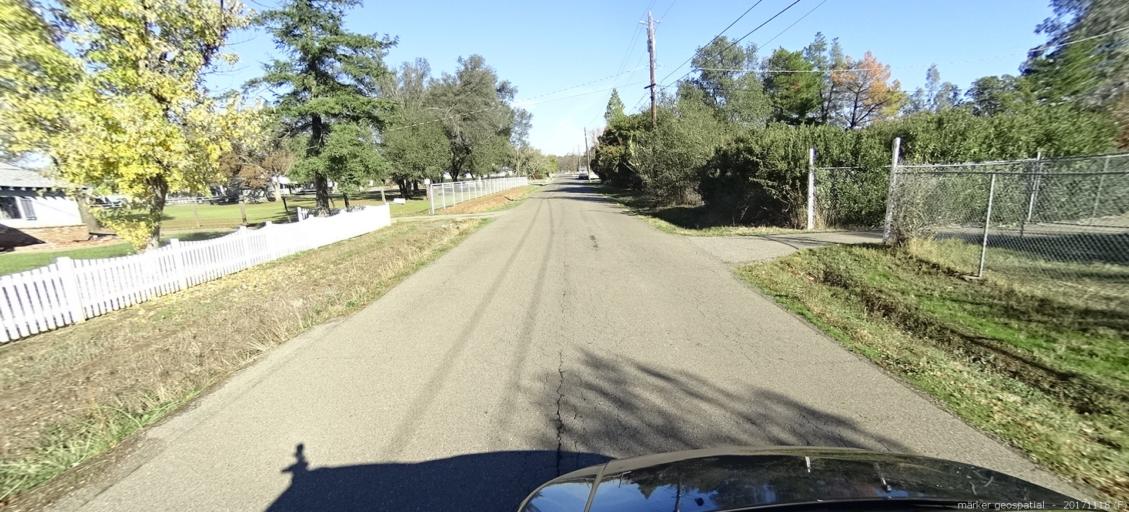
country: US
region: California
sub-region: Shasta County
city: Cottonwood
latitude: 40.3862
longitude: -122.3215
